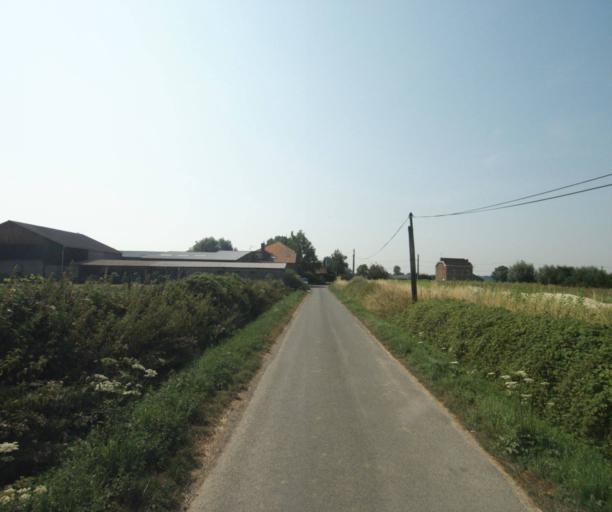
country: FR
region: Nord-Pas-de-Calais
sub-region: Departement du Nord
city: Quesnoy-sur-Deule
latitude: 50.7016
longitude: 2.9977
